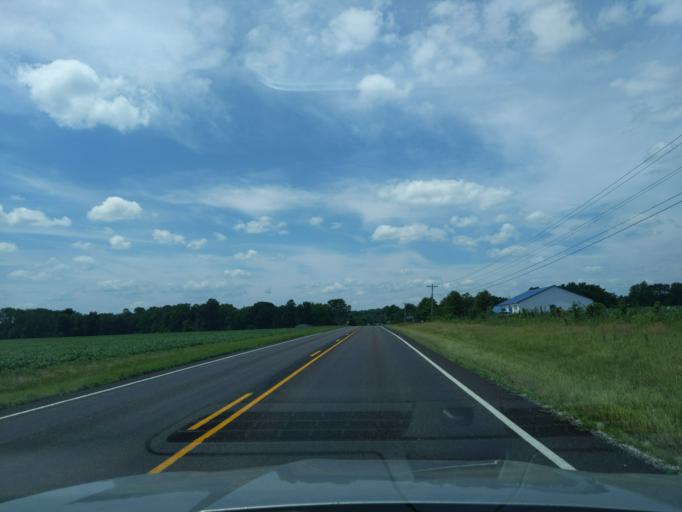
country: US
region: Indiana
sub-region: Decatur County
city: Greensburg
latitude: 39.2891
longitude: -85.4157
